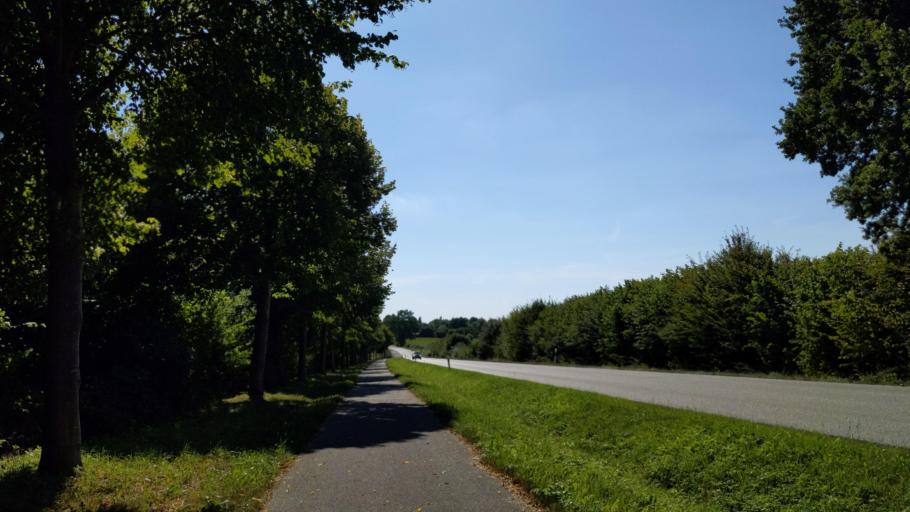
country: DE
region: Mecklenburg-Vorpommern
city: Selmsdorf
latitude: 53.8342
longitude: 10.8972
